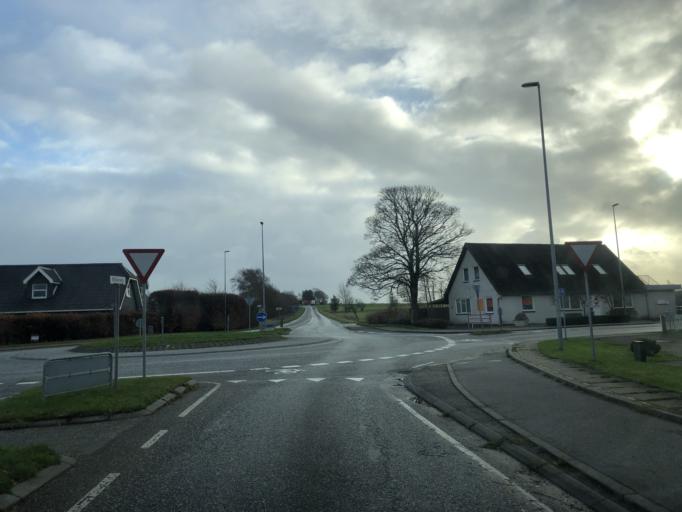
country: DK
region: North Denmark
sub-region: Rebild Kommune
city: Stovring
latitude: 56.8870
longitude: 9.7861
